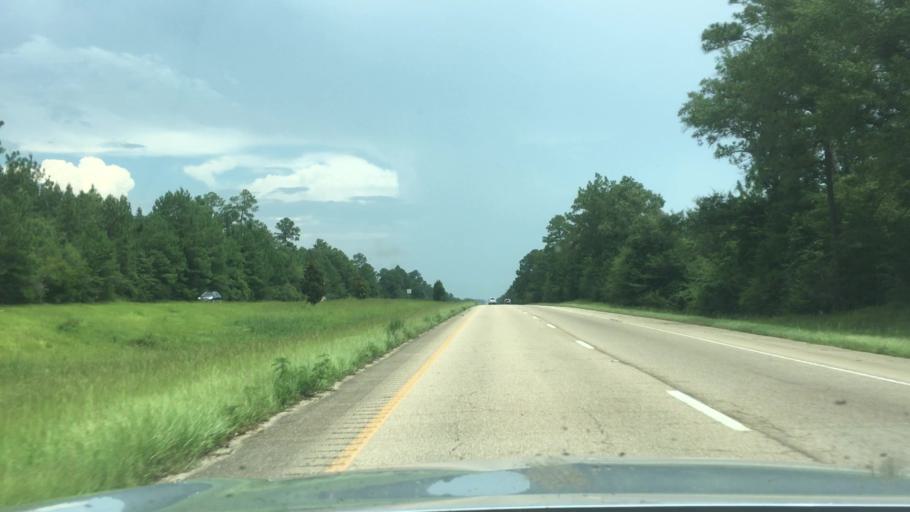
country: US
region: Mississippi
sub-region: Lamar County
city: Lumberton
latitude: 30.9559
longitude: -89.4414
